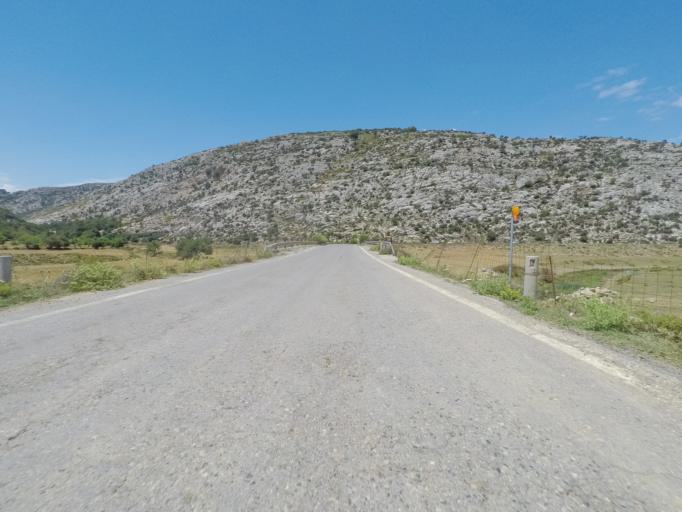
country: GR
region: Crete
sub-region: Nomos Irakleiou
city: Mokhos
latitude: 35.1919
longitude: 25.4322
